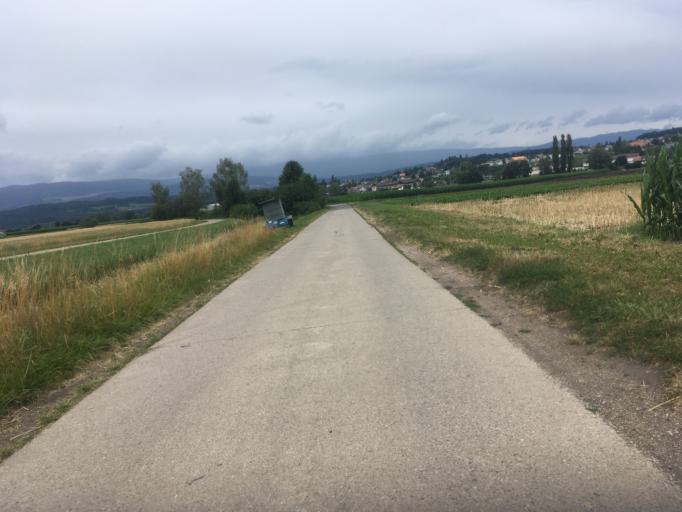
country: CH
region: Bern
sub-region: Seeland District
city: Ins
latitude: 46.9910
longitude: 7.1036
